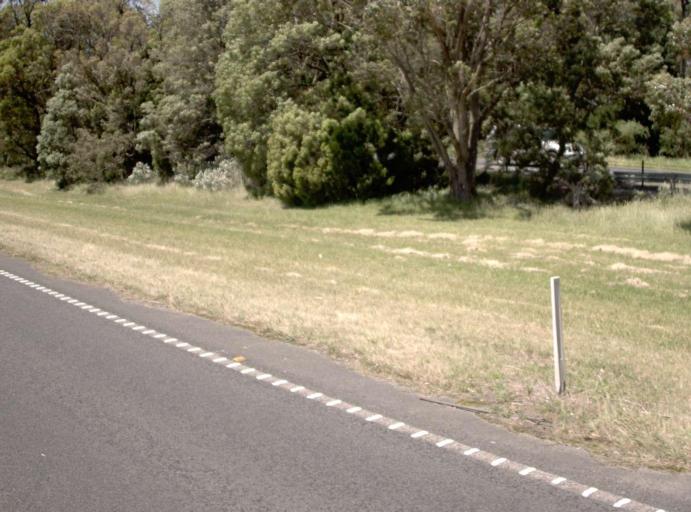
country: AU
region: Victoria
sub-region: Cardinia
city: Garfield
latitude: -38.0704
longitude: 145.6427
